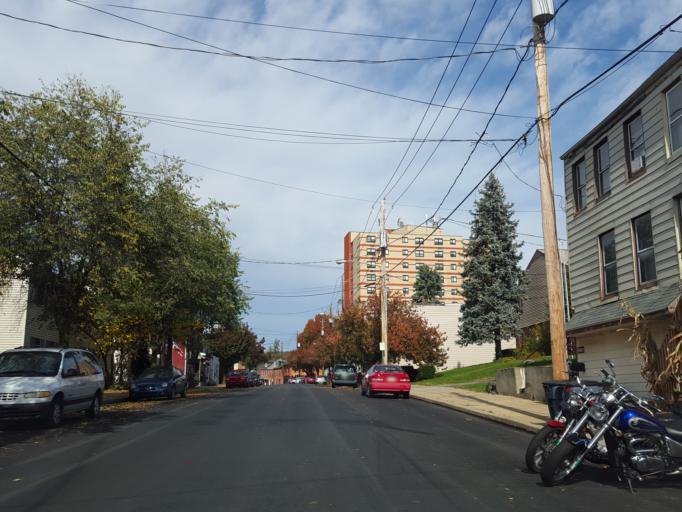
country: US
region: Pennsylvania
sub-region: Lancaster County
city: Columbia
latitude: 40.0288
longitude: -76.4979
